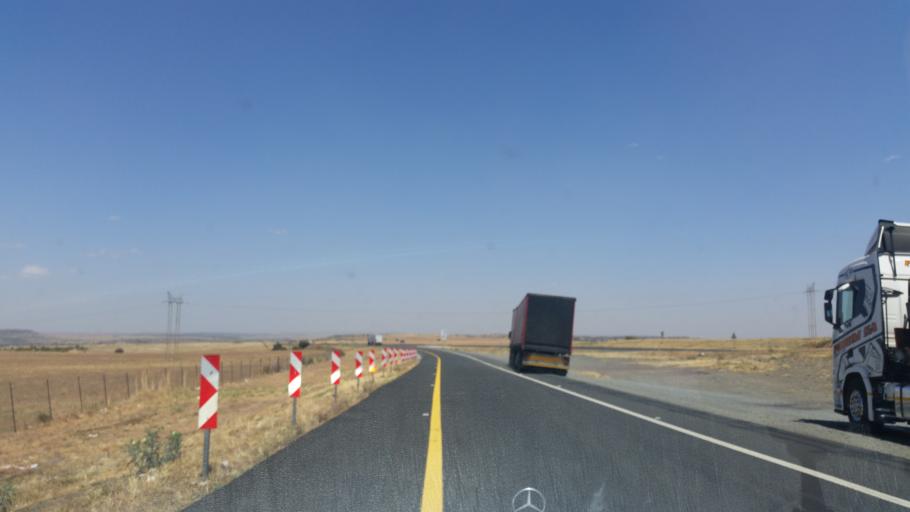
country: ZA
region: Orange Free State
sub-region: Lejweleputswa District Municipality
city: Winburg
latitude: -28.5008
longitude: 26.9970
